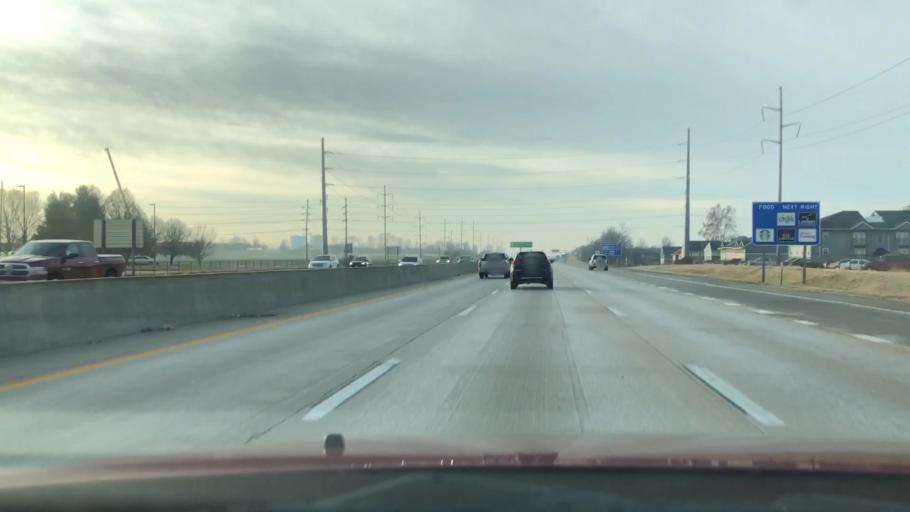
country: US
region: Missouri
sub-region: Greene County
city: Springfield
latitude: 37.1709
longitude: -93.2244
